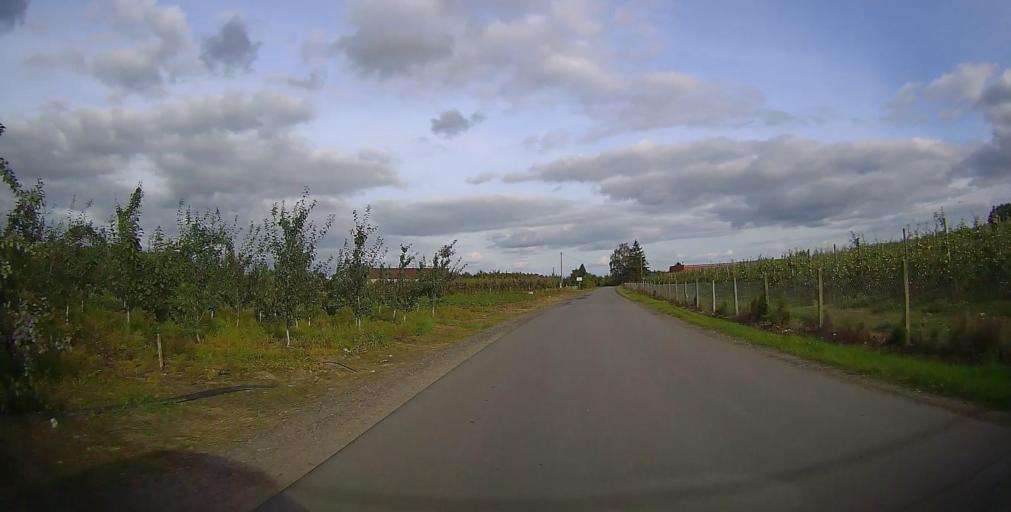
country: PL
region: Masovian Voivodeship
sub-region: Powiat grojecki
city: Jasieniec
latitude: 51.7582
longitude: 20.9421
